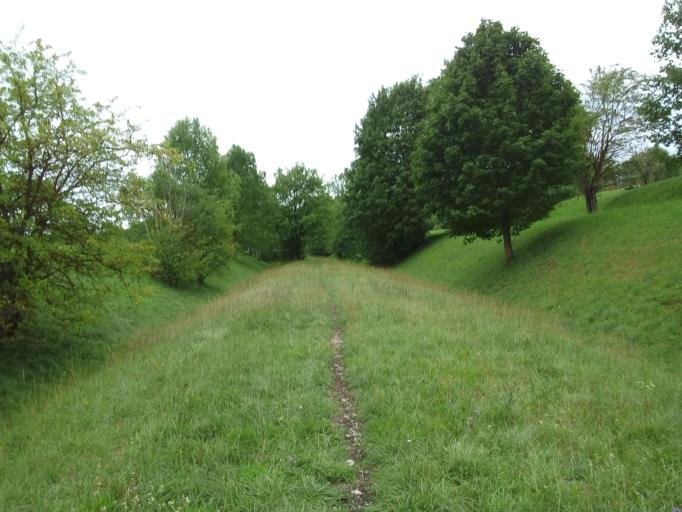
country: DE
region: Bavaria
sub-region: Upper Bavaria
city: Feldkirchen
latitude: 48.1495
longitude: 11.7120
